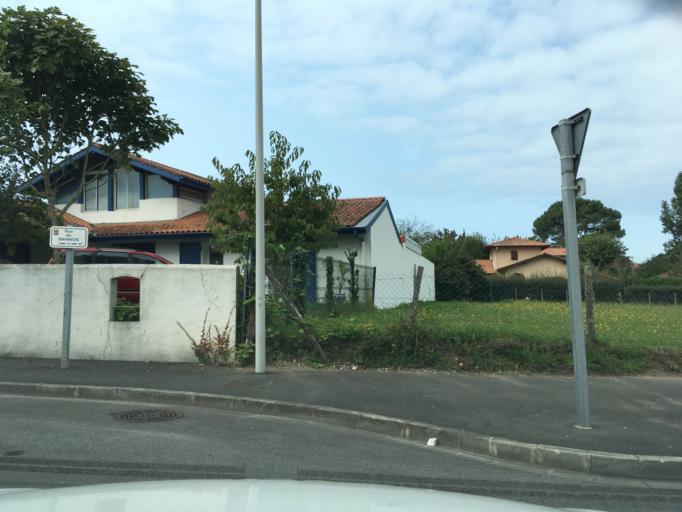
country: FR
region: Aquitaine
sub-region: Departement des Pyrenees-Atlantiques
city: Anglet
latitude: 43.4905
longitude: -1.5165
